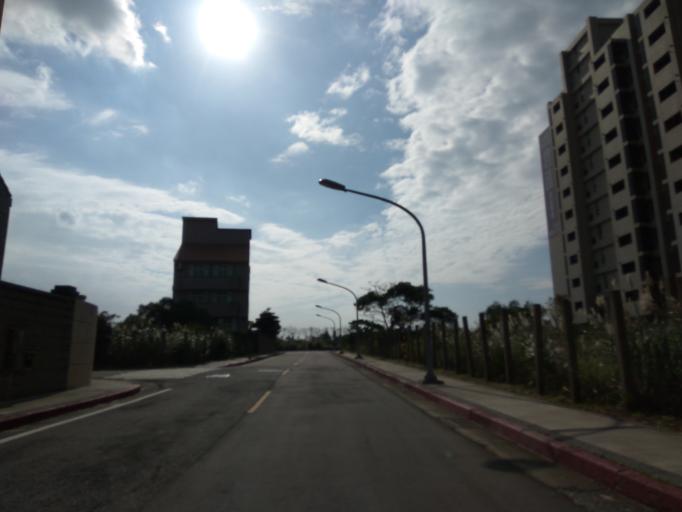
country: TW
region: Taiwan
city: Taoyuan City
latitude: 25.0509
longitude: 121.1752
